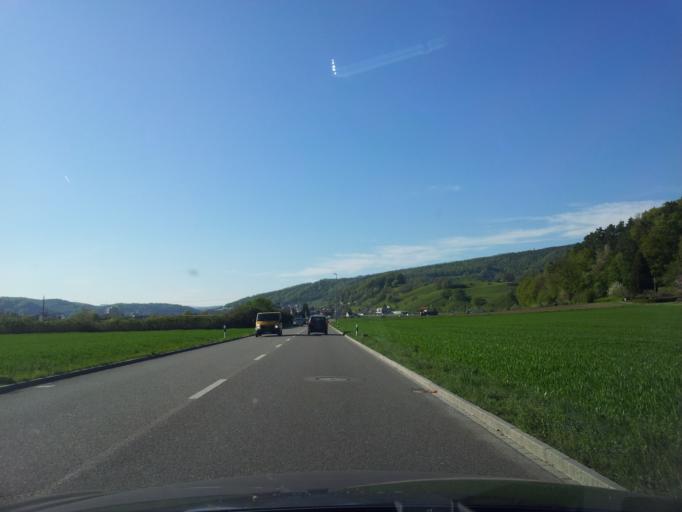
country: CH
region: Aargau
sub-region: Bezirk Baden
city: Wurenlos
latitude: 47.4501
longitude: 8.3535
